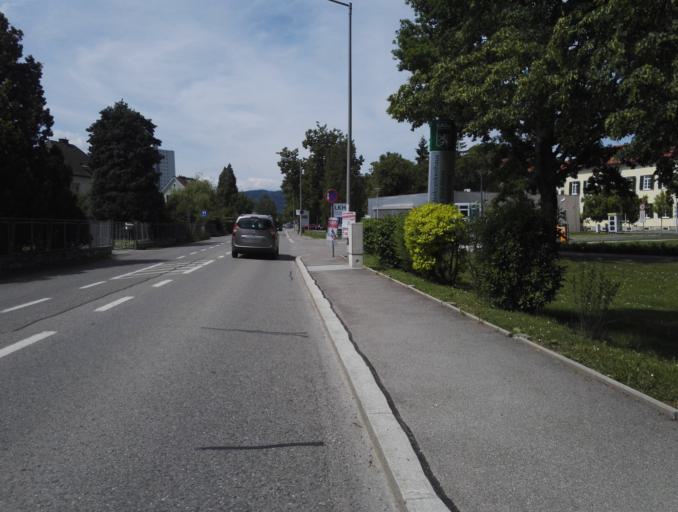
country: AT
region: Styria
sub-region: Graz Stadt
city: Wetzelsdorf
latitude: 47.0371
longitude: 15.4166
